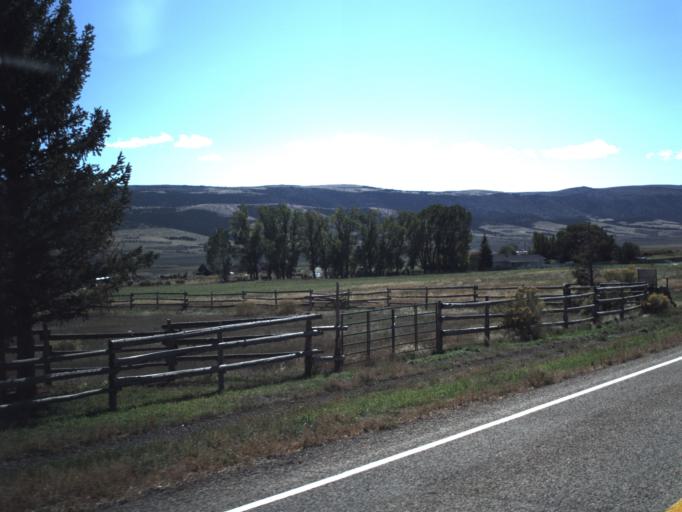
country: US
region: Utah
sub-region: Wayne County
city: Loa
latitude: 38.5055
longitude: -111.8814
